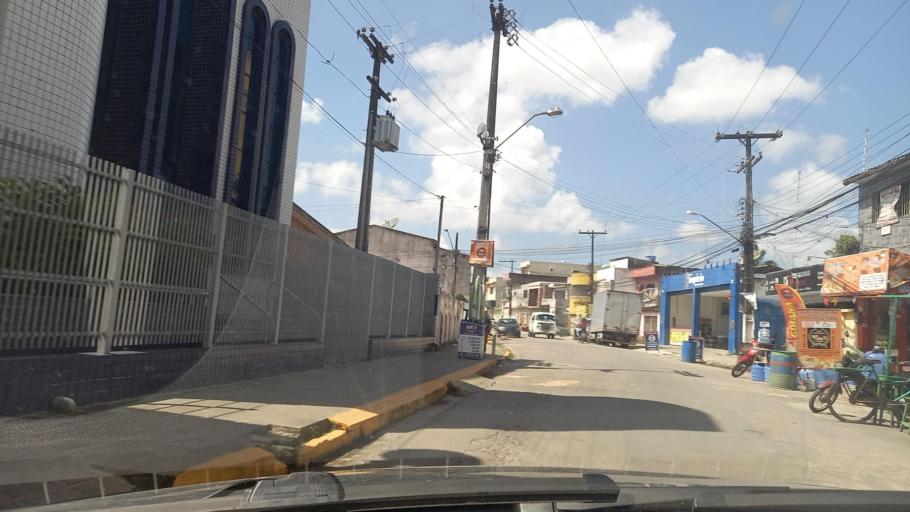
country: BR
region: Pernambuco
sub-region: Goiana
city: Goiana
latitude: -7.5602
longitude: -35.0032
